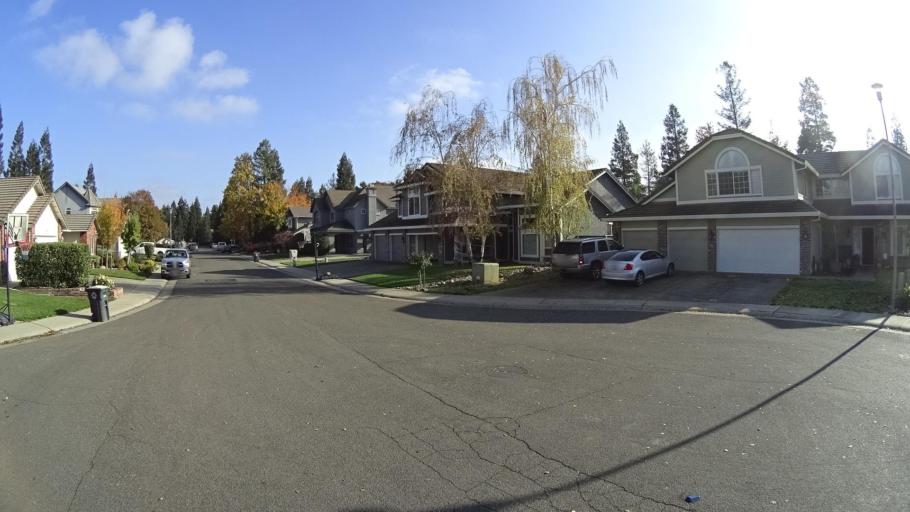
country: US
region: California
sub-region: Sacramento County
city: Elk Grove
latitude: 38.4149
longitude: -121.3573
